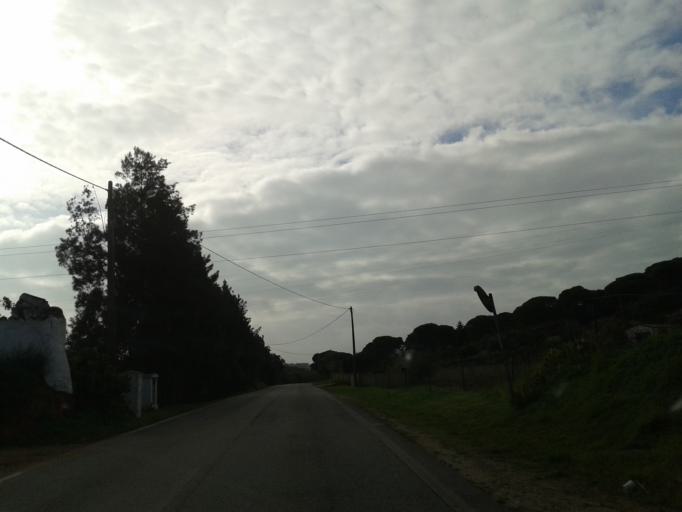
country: PT
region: Faro
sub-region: Vila Real de Santo Antonio
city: Monte Gordo
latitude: 37.1889
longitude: -7.4842
